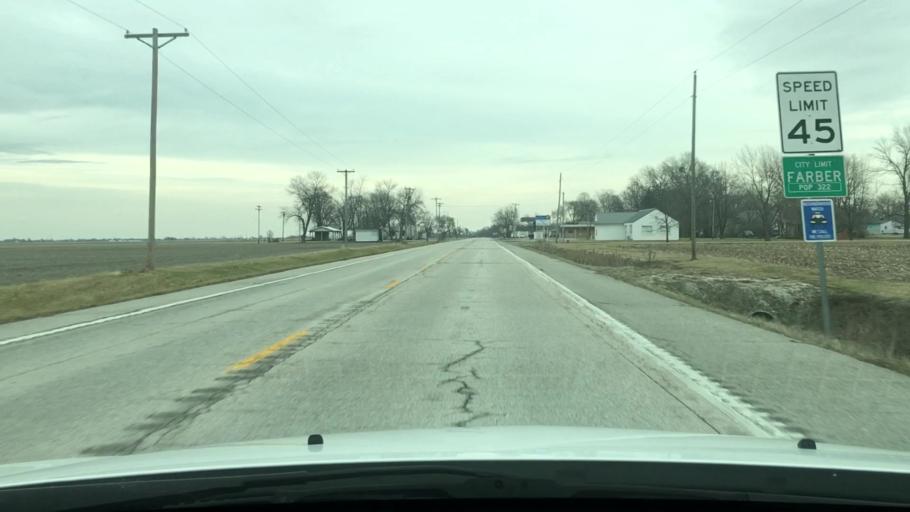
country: US
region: Missouri
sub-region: Audrain County
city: Vandalia
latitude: 39.2793
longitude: -91.5788
